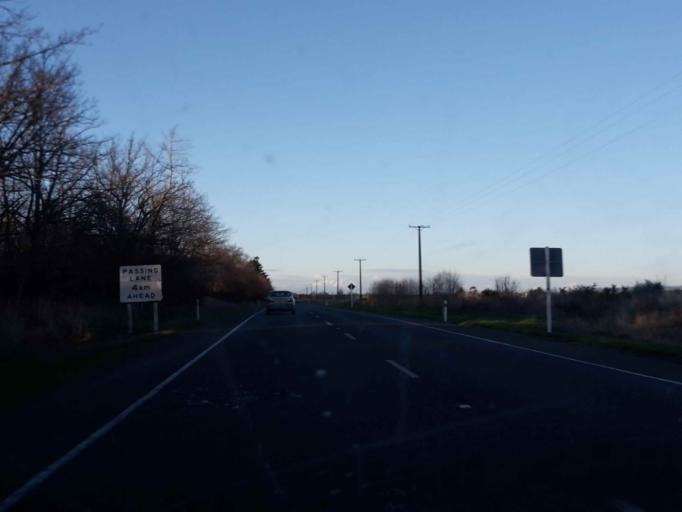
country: NZ
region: Canterbury
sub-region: Selwyn District
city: Burnham
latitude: -43.6280
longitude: 172.2809
